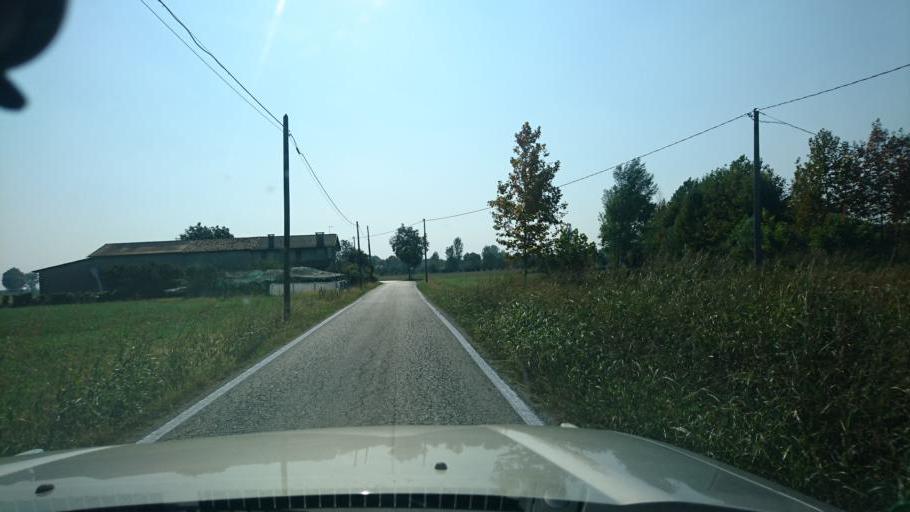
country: IT
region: Veneto
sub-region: Provincia di Vicenza
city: Camisano Vicentino
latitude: 45.5192
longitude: 11.7268
